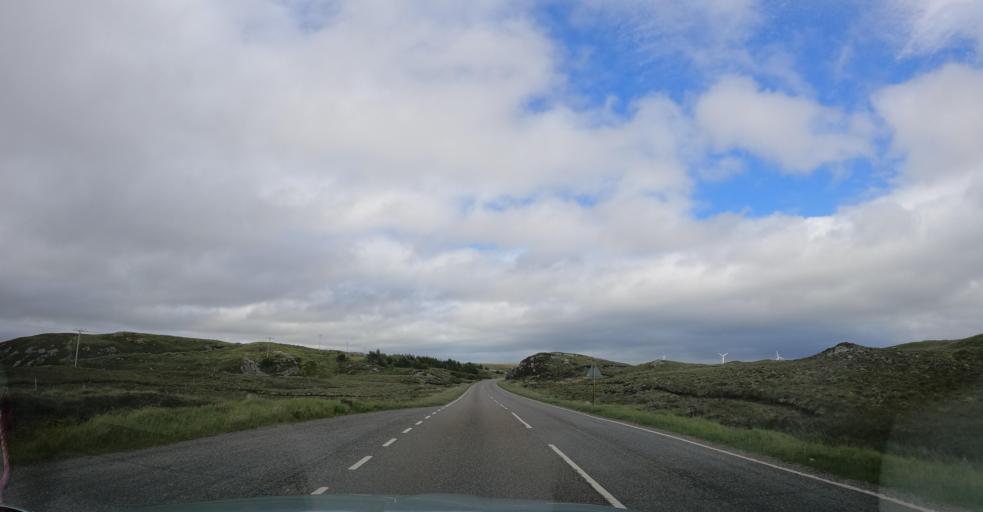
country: GB
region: Scotland
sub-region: Eilean Siar
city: Stornoway
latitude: 58.1732
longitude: -6.4726
